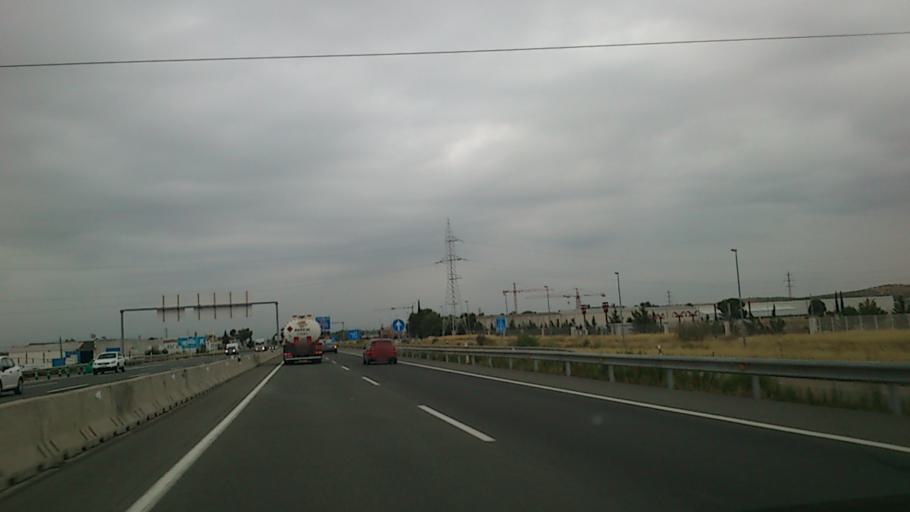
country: ES
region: Aragon
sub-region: Provincia de Zaragoza
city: Villanueva de Gallego
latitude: 41.7431
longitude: -0.8434
